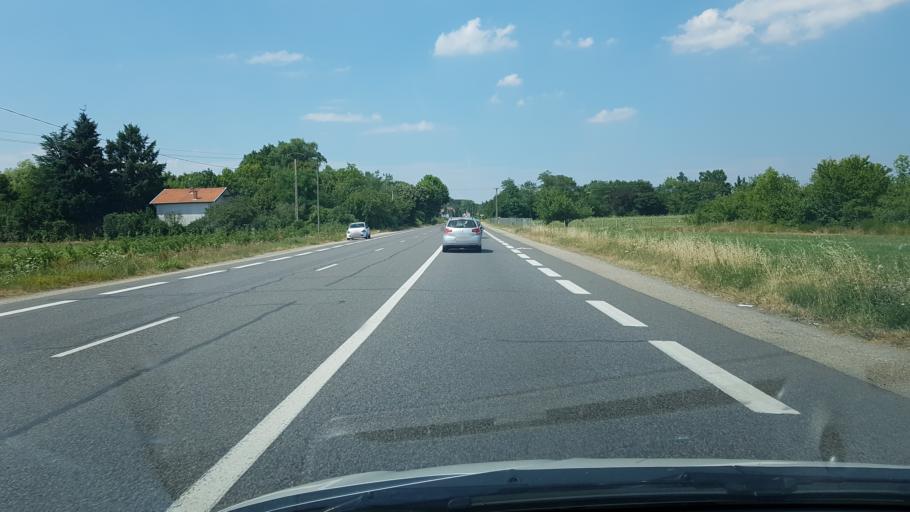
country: FR
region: Rhone-Alpes
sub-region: Departement du Rhone
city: Montagny
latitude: 45.6479
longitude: 4.7515
